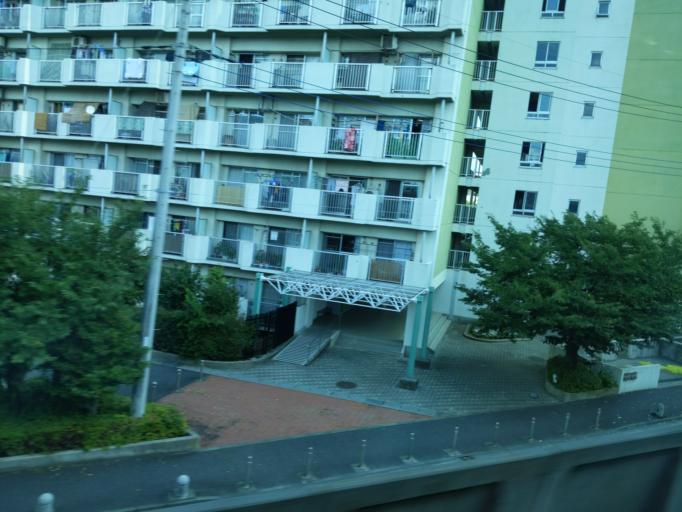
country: JP
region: Tokyo
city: Chofugaoka
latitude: 35.6393
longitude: 139.5247
